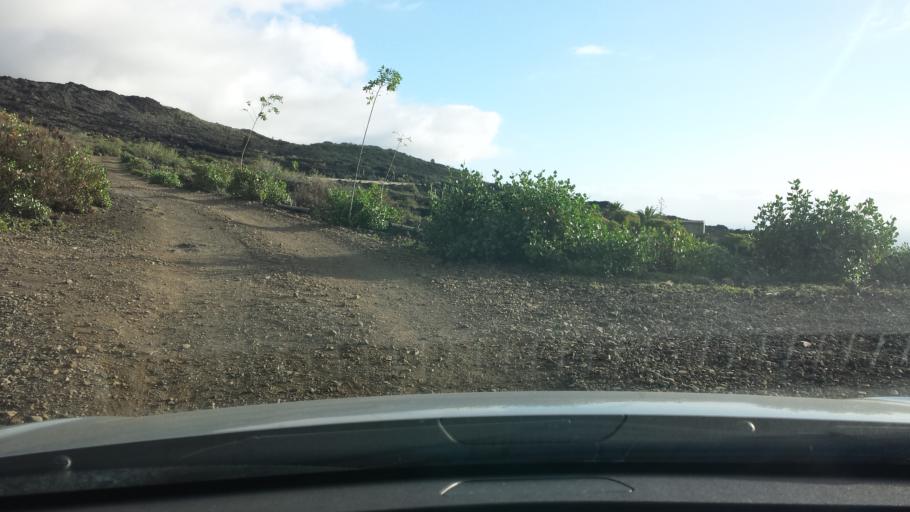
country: ES
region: Canary Islands
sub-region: Provincia de Santa Cruz de Tenerife
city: El Paso
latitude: 28.6050
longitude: -17.8978
